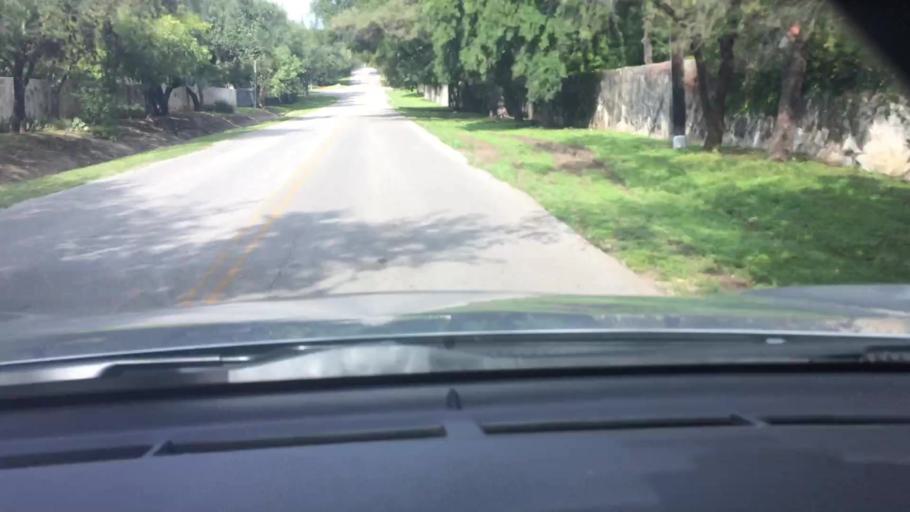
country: US
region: Texas
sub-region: Bexar County
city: Shavano Park
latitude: 29.5542
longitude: -98.5622
